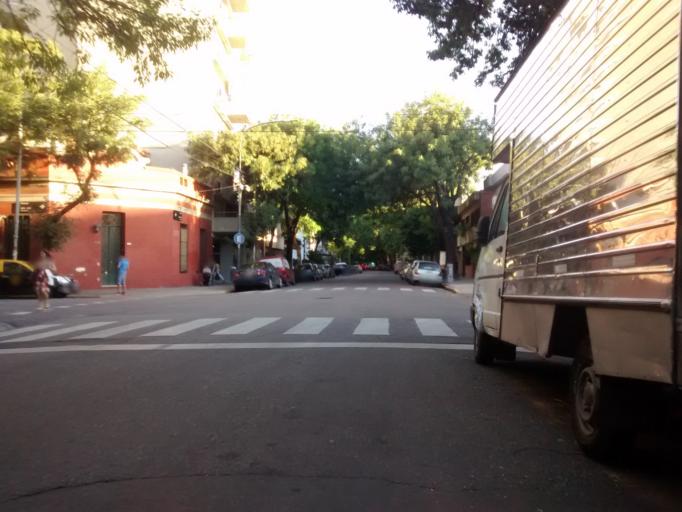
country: AR
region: Buenos Aires F.D.
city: Villa Santa Rita
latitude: -34.6105
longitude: -58.4459
